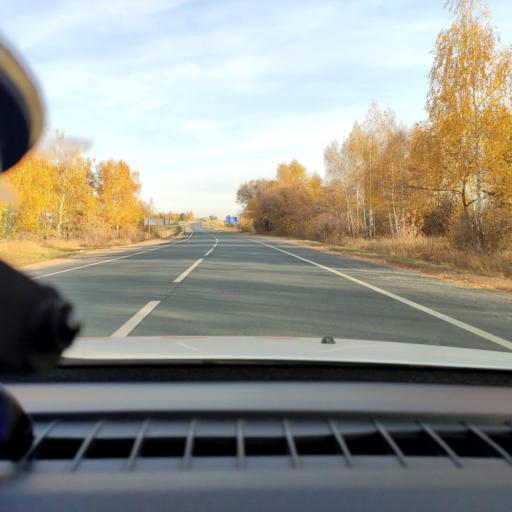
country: RU
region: Samara
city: Bereza
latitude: 53.4825
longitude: 50.1169
